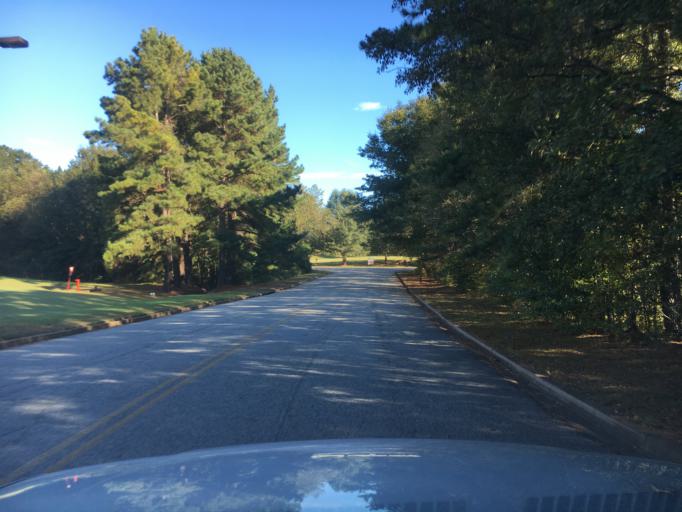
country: US
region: South Carolina
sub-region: Spartanburg County
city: Wellford
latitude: 34.9148
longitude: -82.0997
